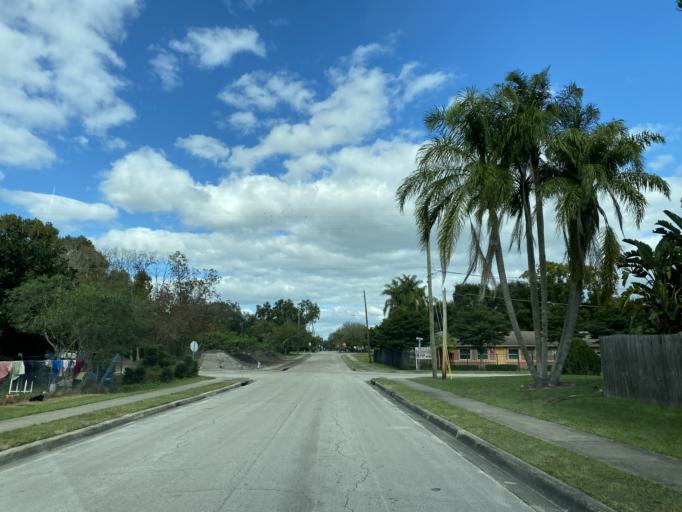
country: US
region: Florida
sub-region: Orange County
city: Holden Heights
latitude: 28.5170
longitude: -81.3908
